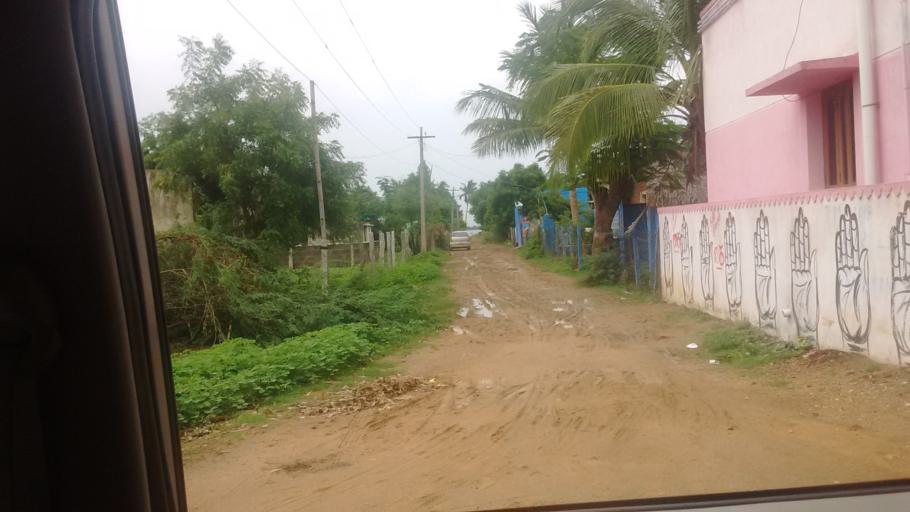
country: IN
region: Tamil Nadu
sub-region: Kancheepuram
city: Madambakkam
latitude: 12.8973
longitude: 80.0305
